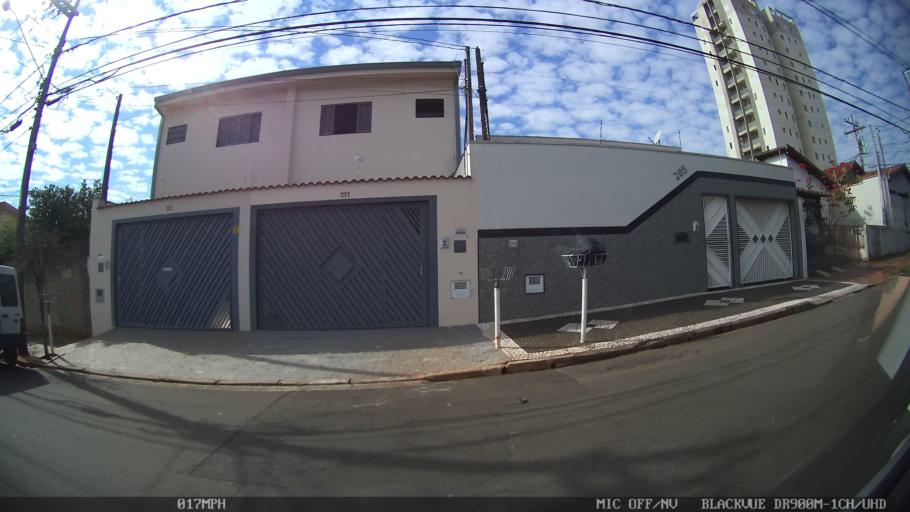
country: BR
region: Sao Paulo
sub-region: Santa Barbara D'Oeste
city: Santa Barbara d'Oeste
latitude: -22.7618
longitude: -47.4030
